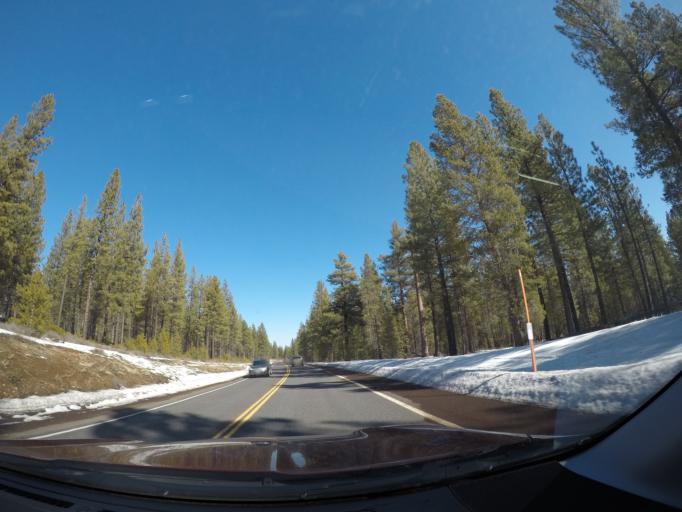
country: US
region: Oregon
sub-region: Deschutes County
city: Three Rivers
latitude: 43.8605
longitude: -121.4922
